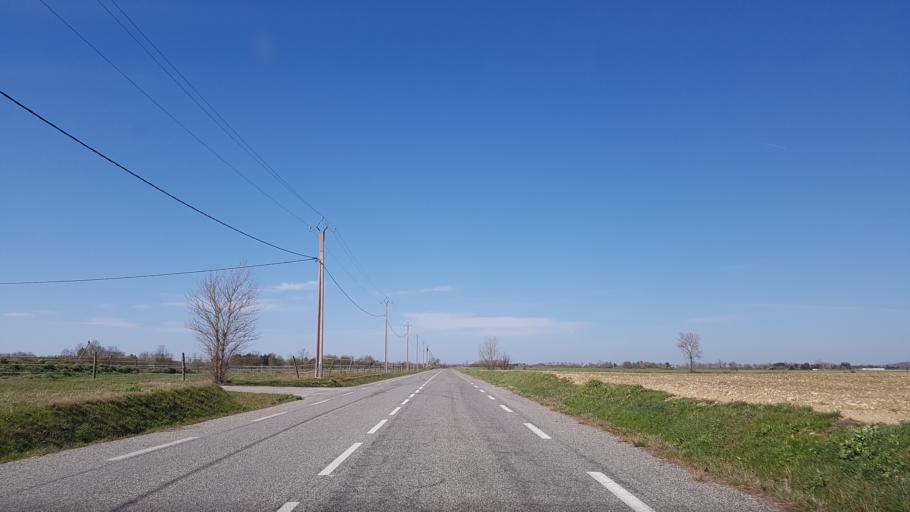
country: FR
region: Midi-Pyrenees
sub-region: Departement de l'Ariege
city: Mazeres
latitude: 43.2278
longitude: 1.6770
